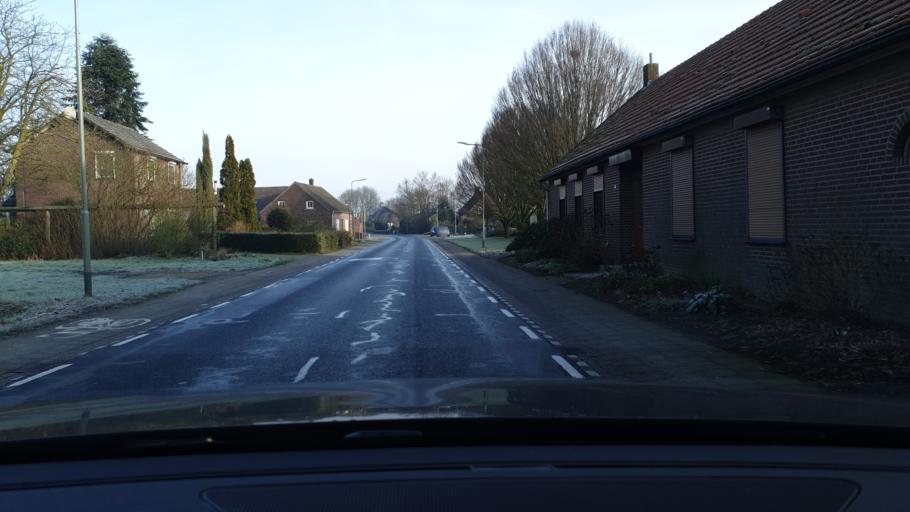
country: NL
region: Limburg
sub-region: Gemeente Peel en Maas
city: Maasbree
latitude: 51.3959
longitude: 6.0167
